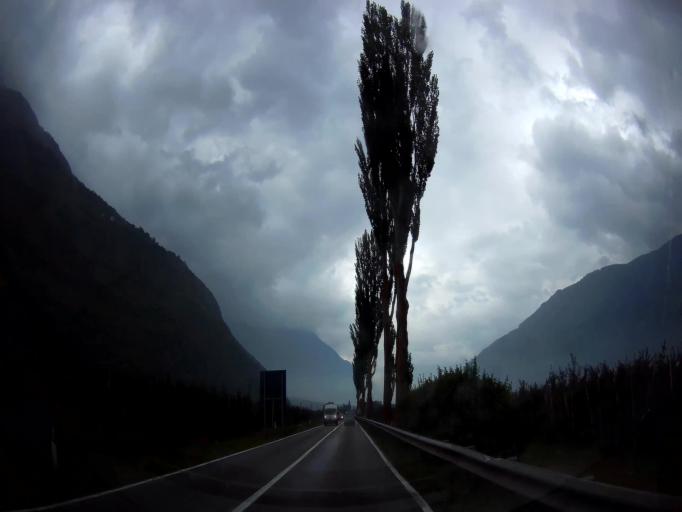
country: IT
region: Trentino-Alto Adige
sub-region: Bolzano
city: Plaus
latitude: 46.6588
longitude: 11.0331
